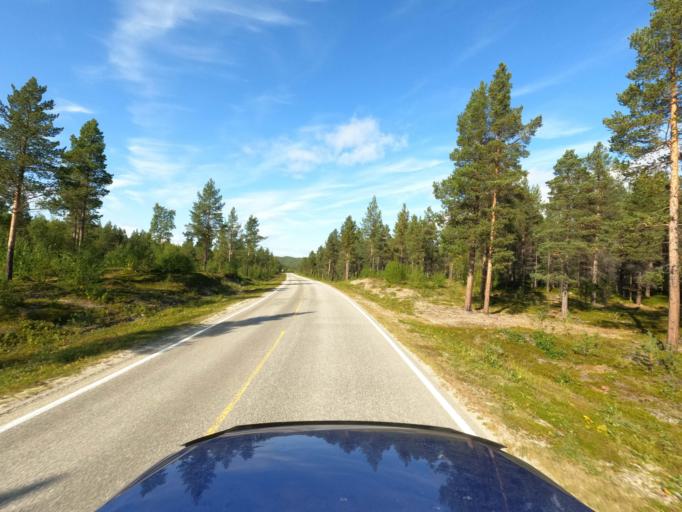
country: NO
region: Finnmark Fylke
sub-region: Porsanger
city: Lakselv
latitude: 69.8216
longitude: 25.1558
